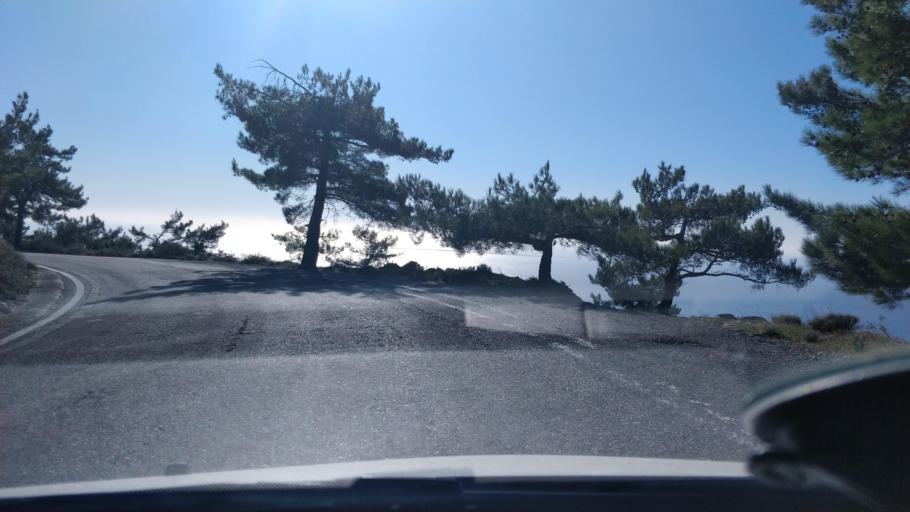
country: GR
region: Crete
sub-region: Nomos Lasithiou
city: Gra Liyia
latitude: 35.0443
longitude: 25.6332
